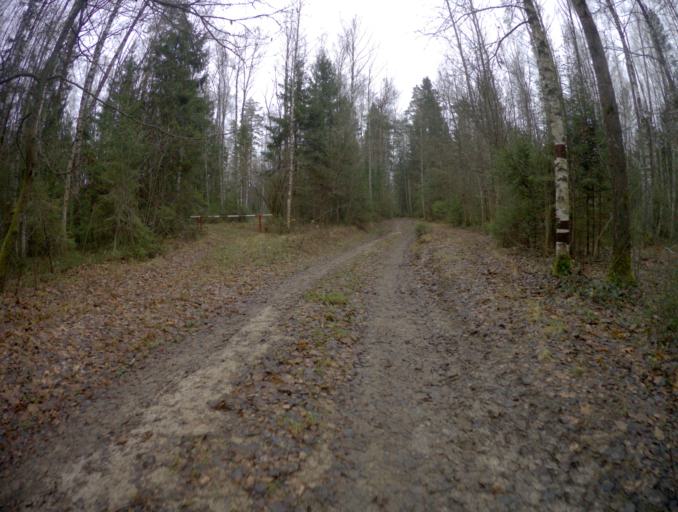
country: RU
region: Vladimir
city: Kommunar
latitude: 56.0326
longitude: 40.5138
